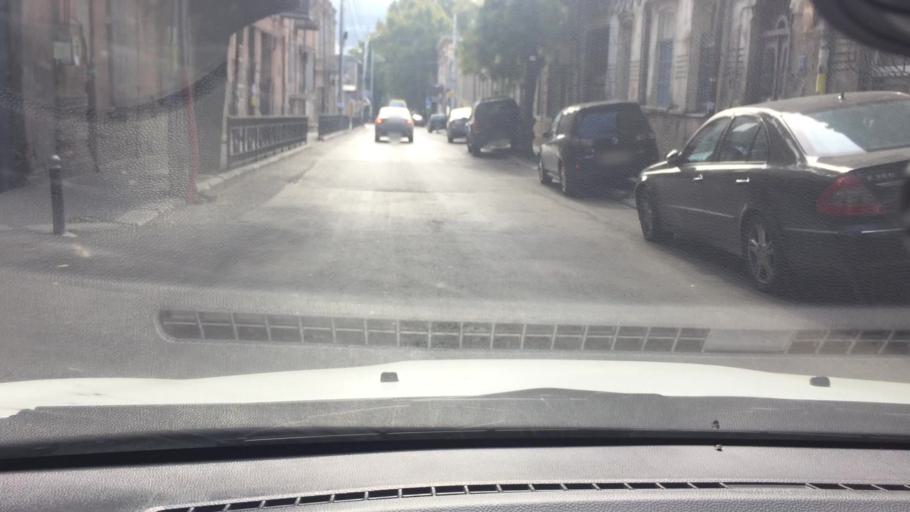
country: GE
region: T'bilisi
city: Tbilisi
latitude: 41.7087
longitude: 44.8033
